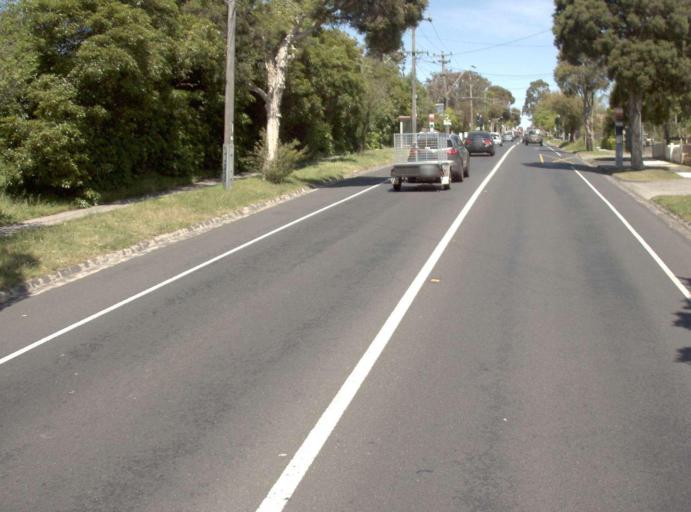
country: AU
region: Victoria
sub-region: Whitehorse
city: Blackburn North
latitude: -37.8054
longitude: 145.1588
